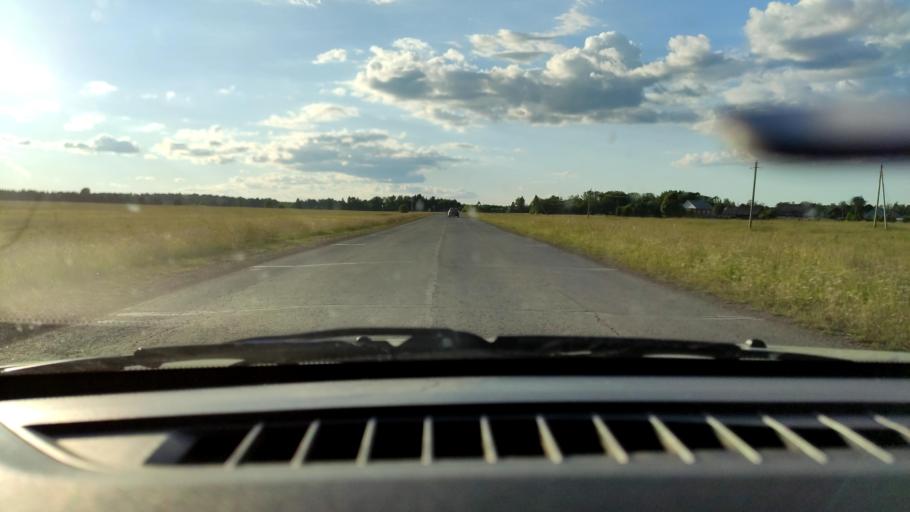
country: RU
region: Perm
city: Uinskoye
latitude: 57.0755
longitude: 56.5586
